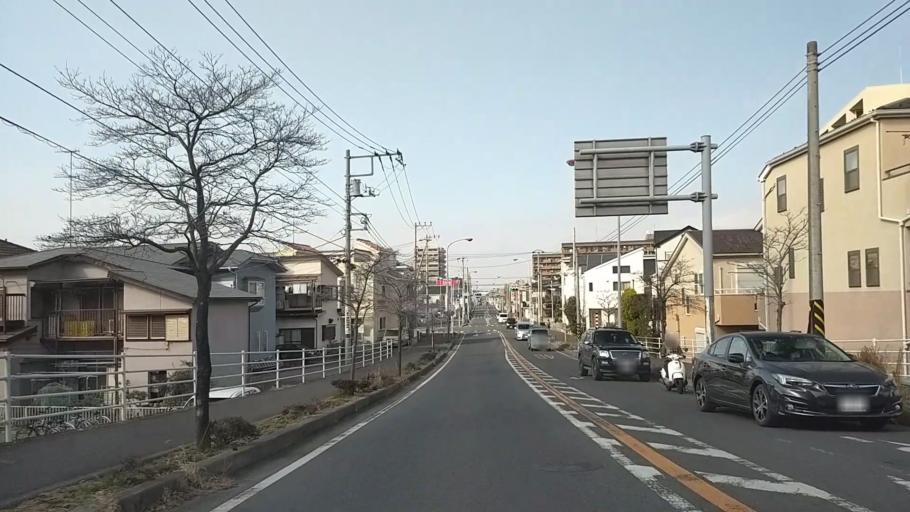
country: JP
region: Kanagawa
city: Chigasaki
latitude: 35.3372
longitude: 139.4141
